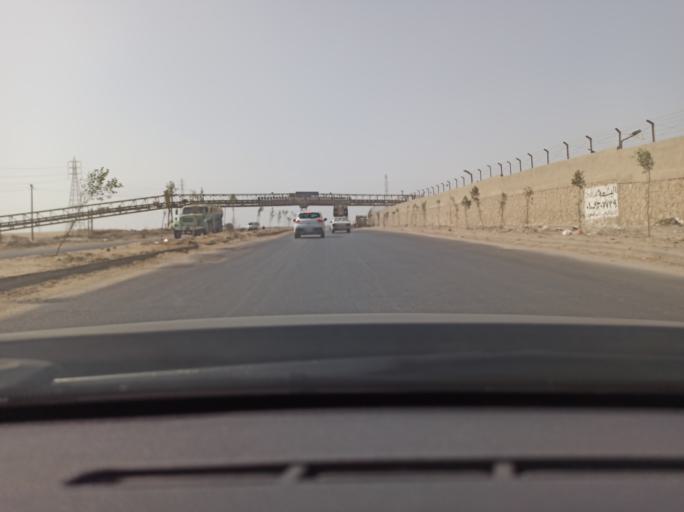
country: EG
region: Muhafazat al Qahirah
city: Halwan
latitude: 29.7934
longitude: 31.3487
